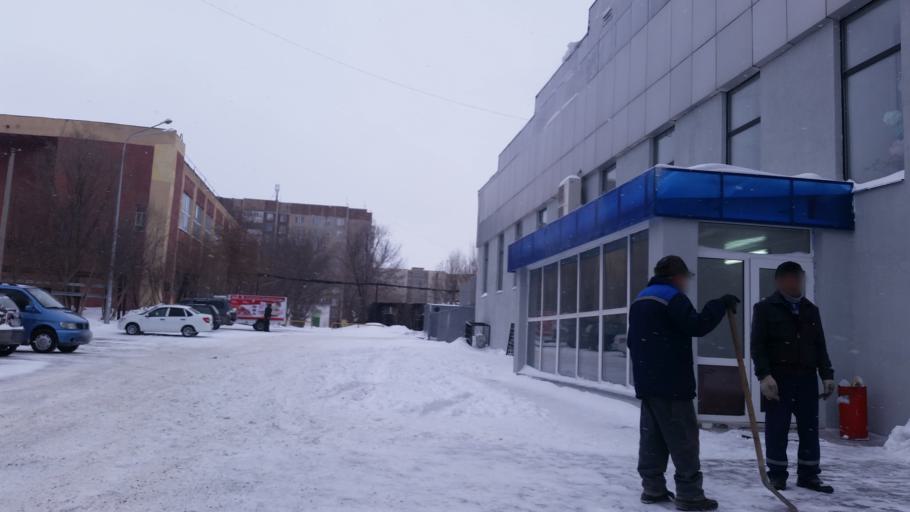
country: KZ
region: Qaraghandy
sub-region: Qaraghandy Qalasy
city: Karagandy
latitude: 49.7750
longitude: 73.1513
